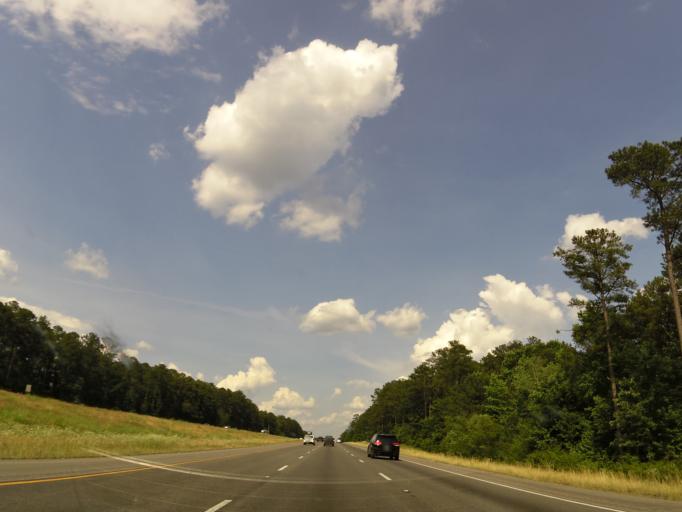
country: US
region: Alabama
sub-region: Tuscaloosa County
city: Coaling
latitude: 33.1849
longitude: -87.3384
